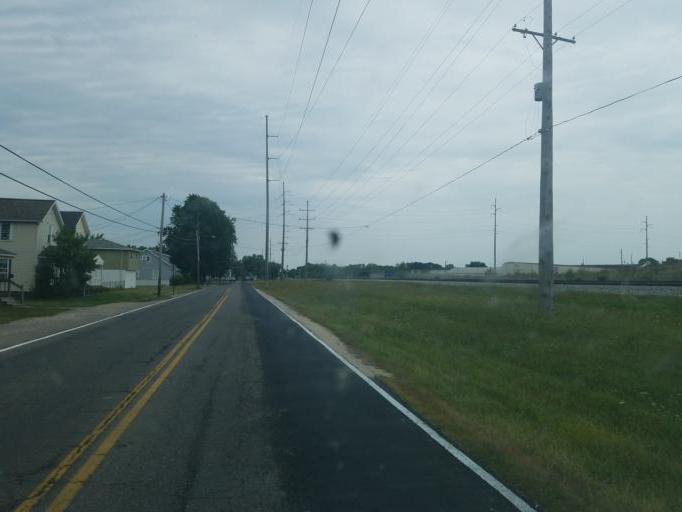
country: US
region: Ohio
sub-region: Marion County
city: Marion
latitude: 40.5688
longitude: -83.1439
